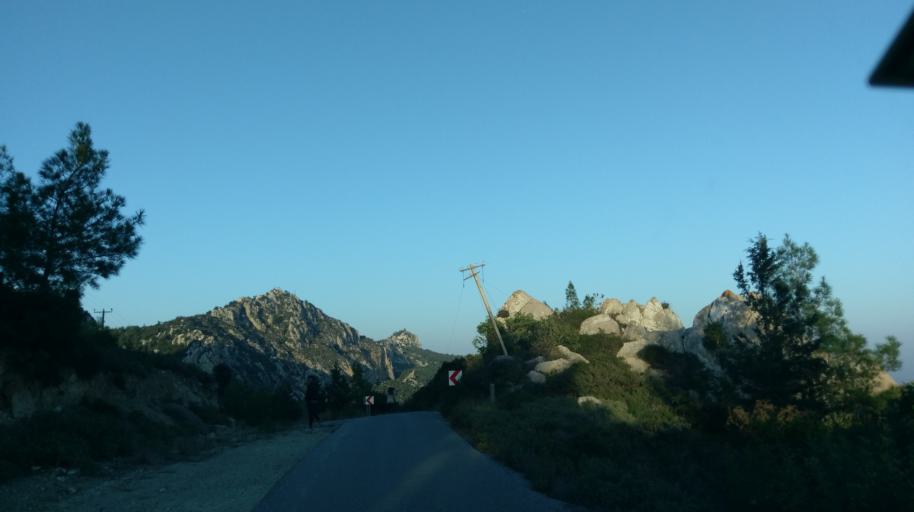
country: CY
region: Ammochostos
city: Trikomo
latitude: 35.3954
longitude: 33.9071
